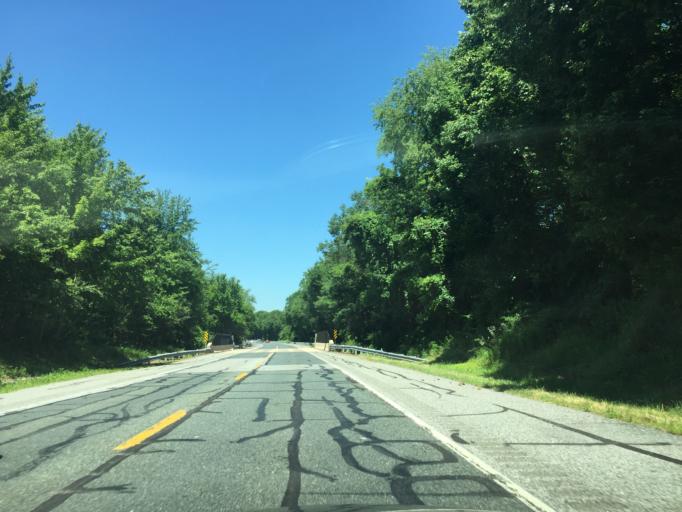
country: US
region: Maryland
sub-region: Harford County
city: Jarrettsville
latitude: 39.5832
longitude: -76.4533
